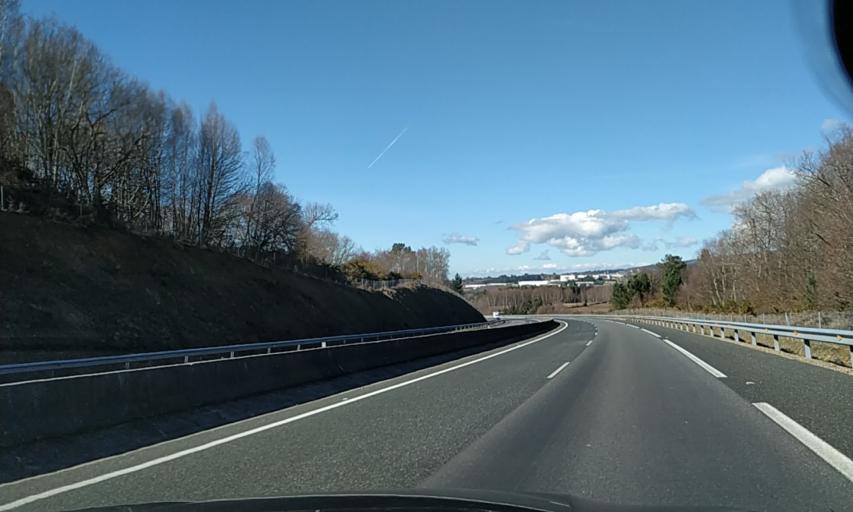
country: ES
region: Galicia
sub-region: Provincia de Pontevedra
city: Lalin
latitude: 42.6574
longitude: -8.1404
